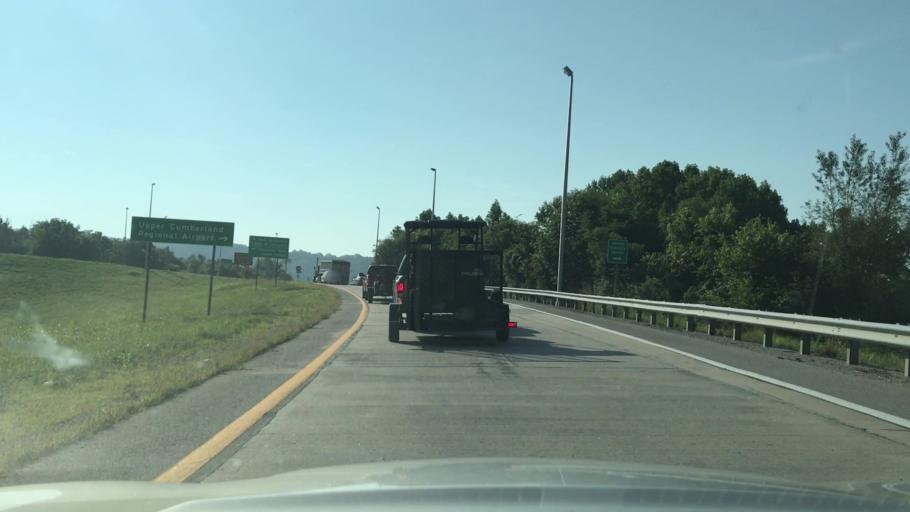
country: US
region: Tennessee
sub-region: Putnam County
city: Cookeville
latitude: 36.1338
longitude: -85.4816
